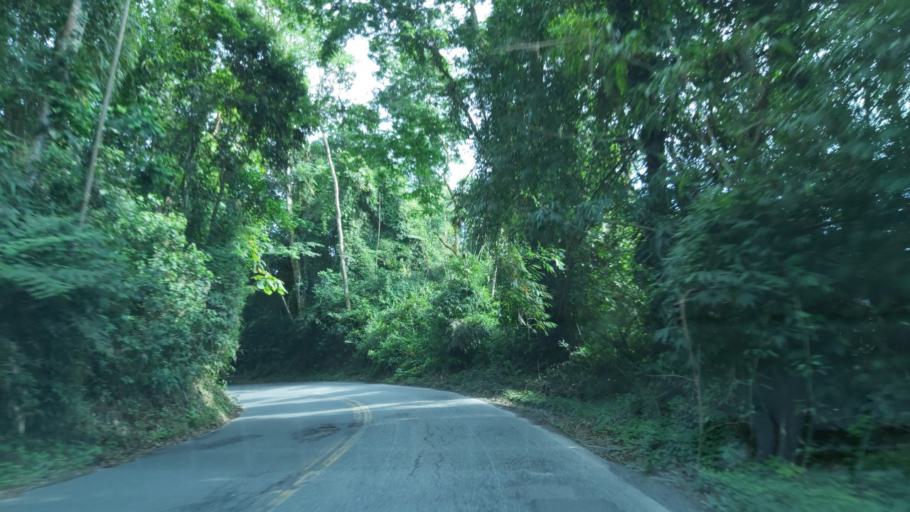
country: BR
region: Sao Paulo
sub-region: Juquia
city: Juquia
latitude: -24.0957
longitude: -47.6148
